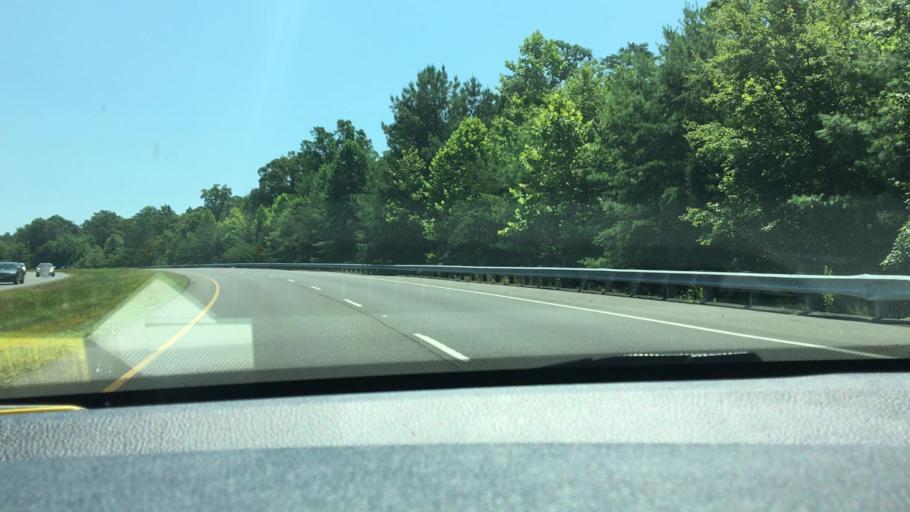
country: US
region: Virginia
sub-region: Prince William County
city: Buckhall
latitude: 38.6984
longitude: -77.4049
